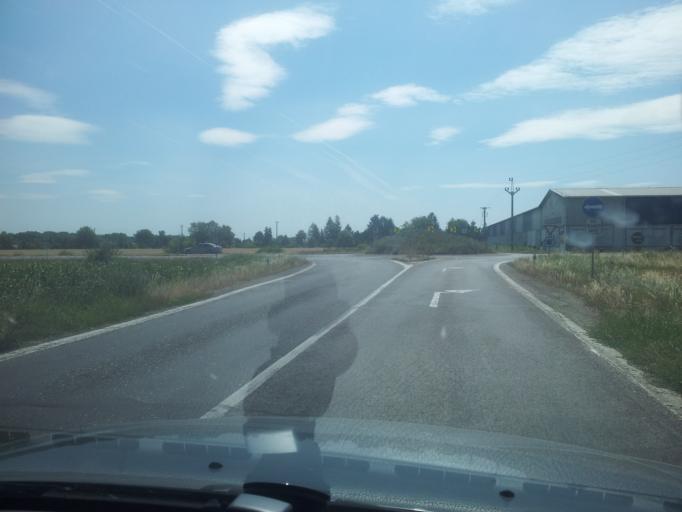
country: SK
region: Nitriansky
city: Zeliezovce
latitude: 48.1136
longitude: 18.6231
